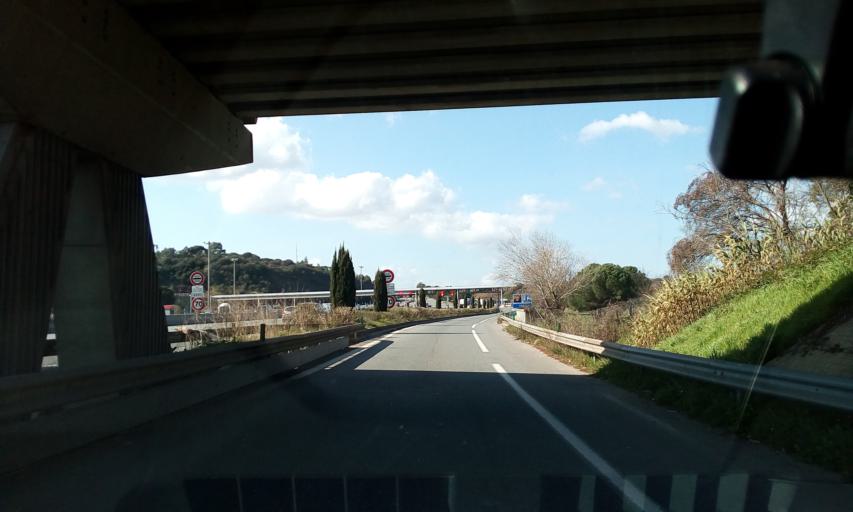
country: FR
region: Provence-Alpes-Cote d'Azur
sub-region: Departement du Var
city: Frejus
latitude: 43.4701
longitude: 6.7328
